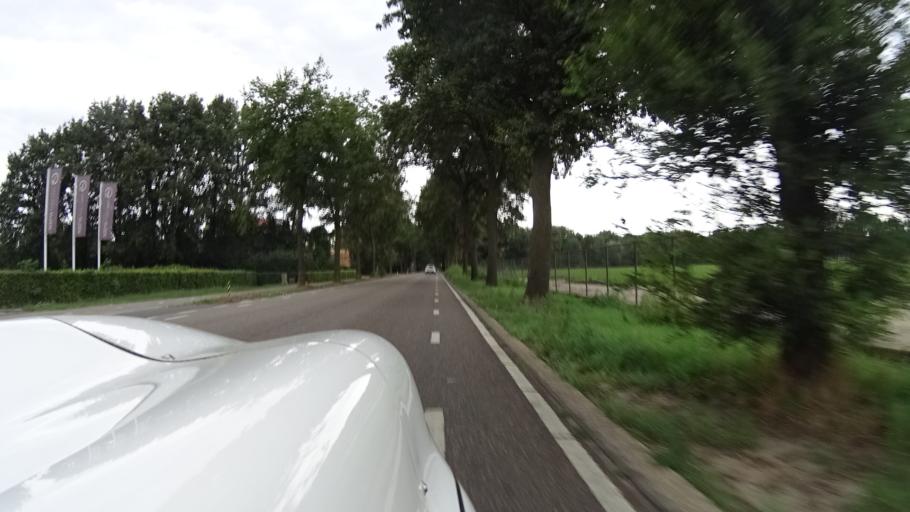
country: NL
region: North Brabant
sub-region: Gemeente Veghel
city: Erp
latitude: 51.6205
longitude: 5.6086
